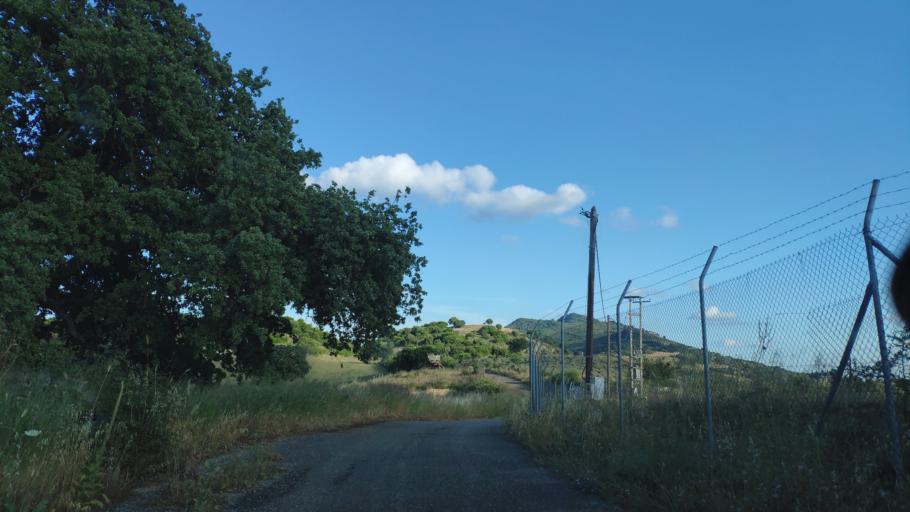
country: GR
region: West Greece
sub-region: Nomos Aitolias kai Akarnanias
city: Fitiai
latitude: 38.6783
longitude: 21.1877
